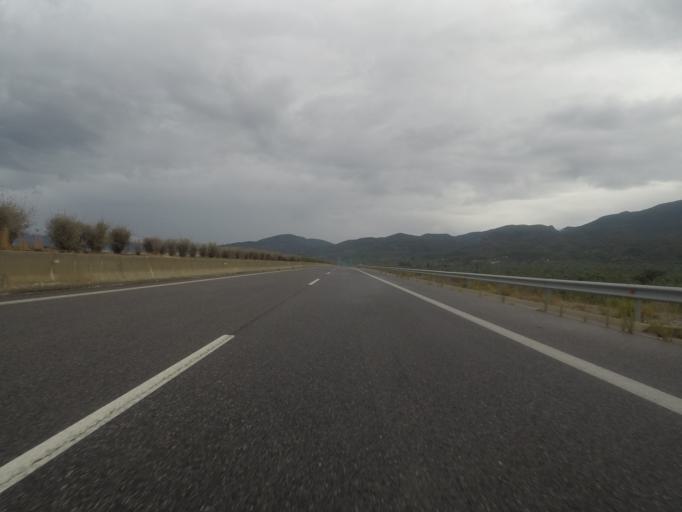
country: GR
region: Peloponnese
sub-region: Nomos Messinias
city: Meligalas
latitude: 37.2366
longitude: 22.0160
